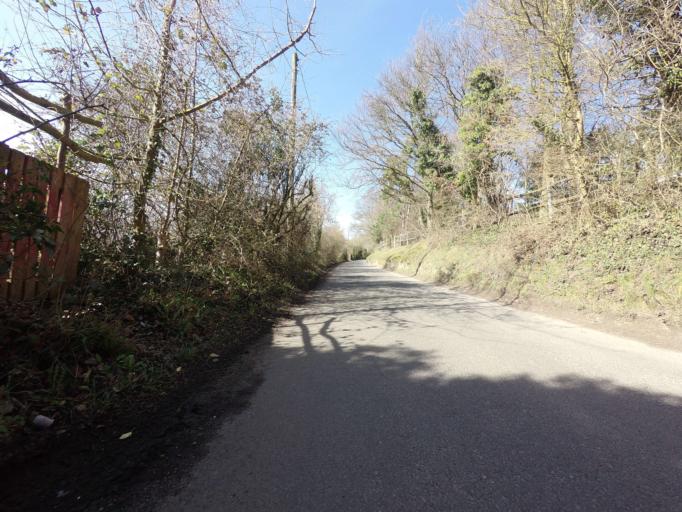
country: GB
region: England
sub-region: Kent
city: Eynsford
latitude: 51.3725
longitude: 0.2047
